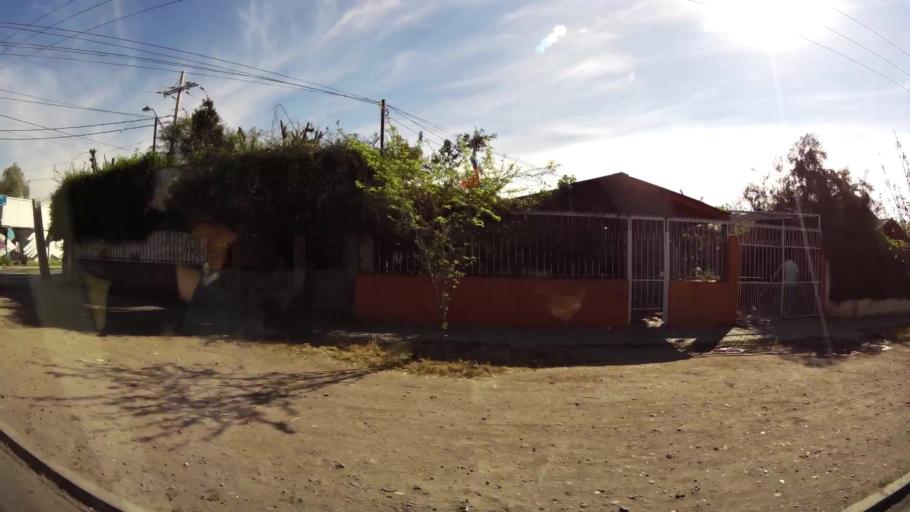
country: CL
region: Santiago Metropolitan
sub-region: Provincia de Santiago
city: La Pintana
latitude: -33.5285
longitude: -70.6242
